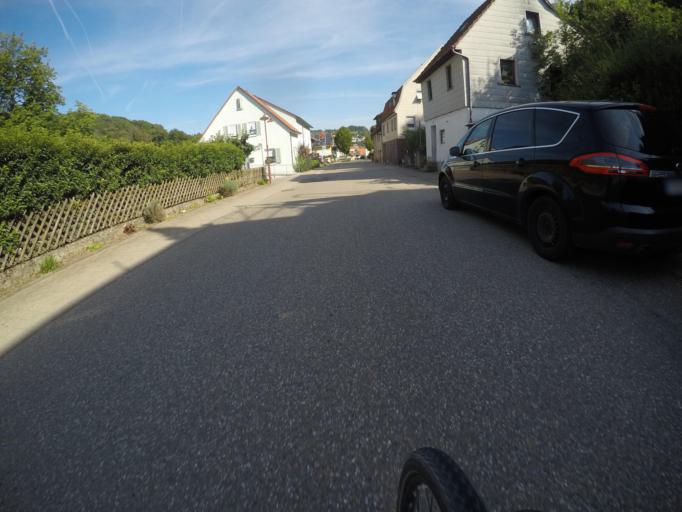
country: DE
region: Baden-Wuerttemberg
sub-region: Karlsruhe Region
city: Monsheim
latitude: 48.8822
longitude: 8.9004
